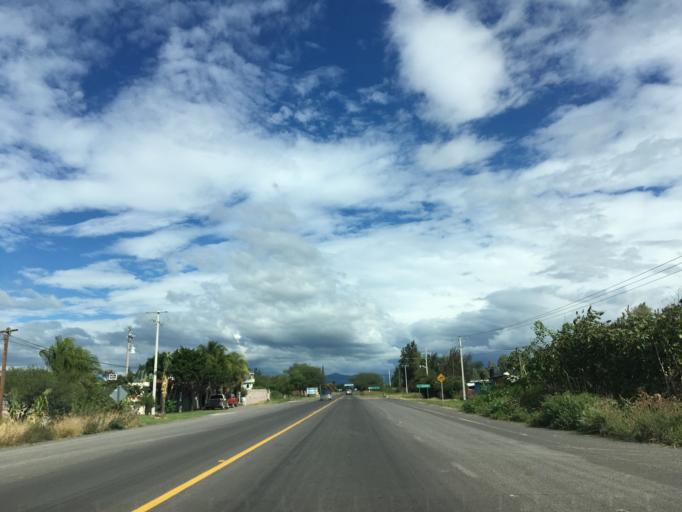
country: MX
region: Michoacan
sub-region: Cuitzeo
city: Cuamio
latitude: 20.0764
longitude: -101.1335
